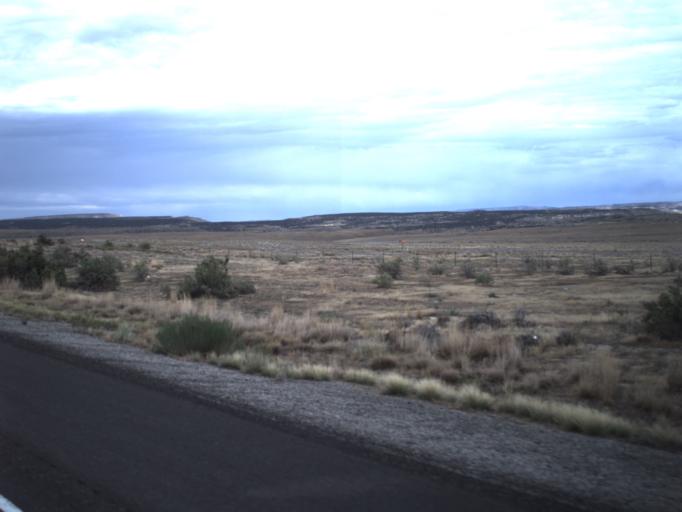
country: US
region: Colorado
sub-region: Mesa County
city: Loma
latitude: 39.1020
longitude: -109.1988
